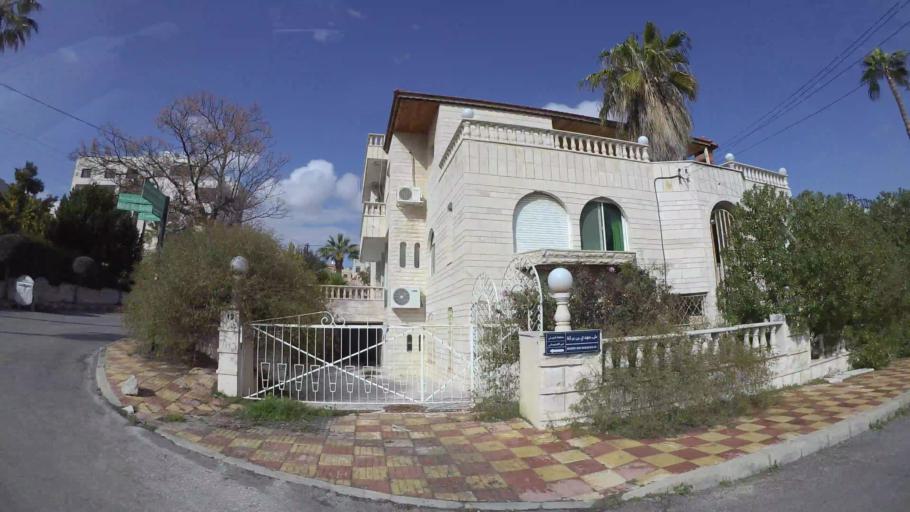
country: JO
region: Amman
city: Amman
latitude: 31.9692
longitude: 35.8902
